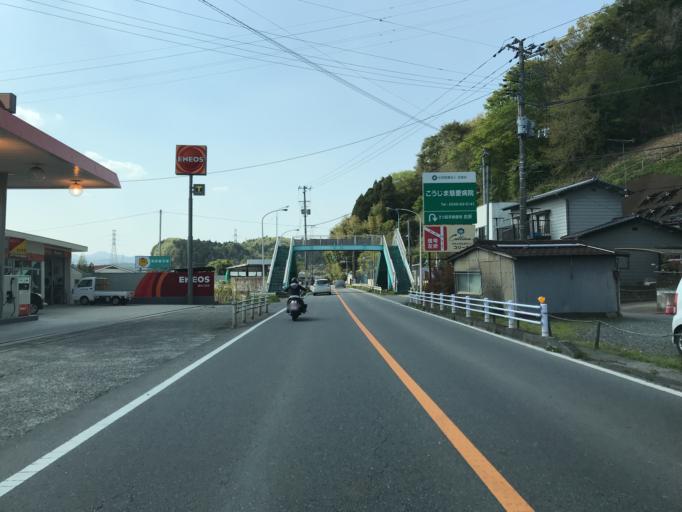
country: JP
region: Ibaraki
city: Kitaibaraki
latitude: 36.9277
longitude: 140.7771
